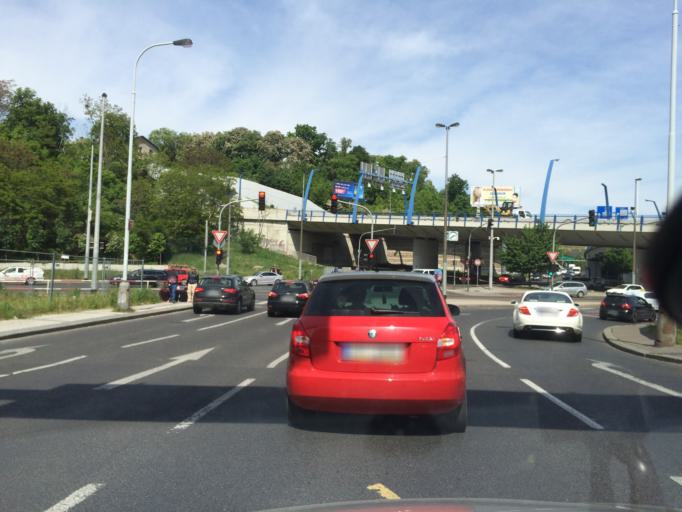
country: CZ
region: Praha
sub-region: Praha 1
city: Mala Strana
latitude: 50.0718
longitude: 14.3972
